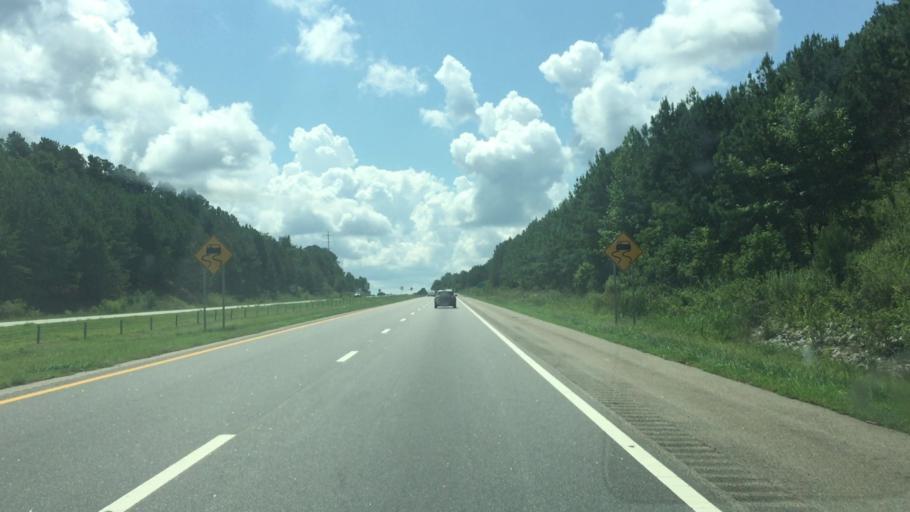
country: US
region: North Carolina
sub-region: Richmond County
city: Cordova
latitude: 34.9424
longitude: -79.8444
